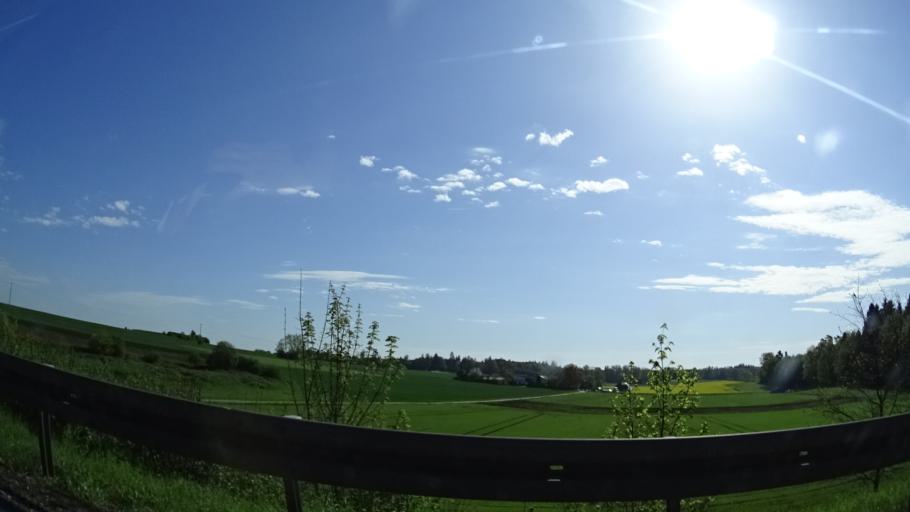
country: DE
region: Baden-Wuerttemberg
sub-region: Regierungsbezirk Stuttgart
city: Motzingen
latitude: 48.5189
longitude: 8.7765
